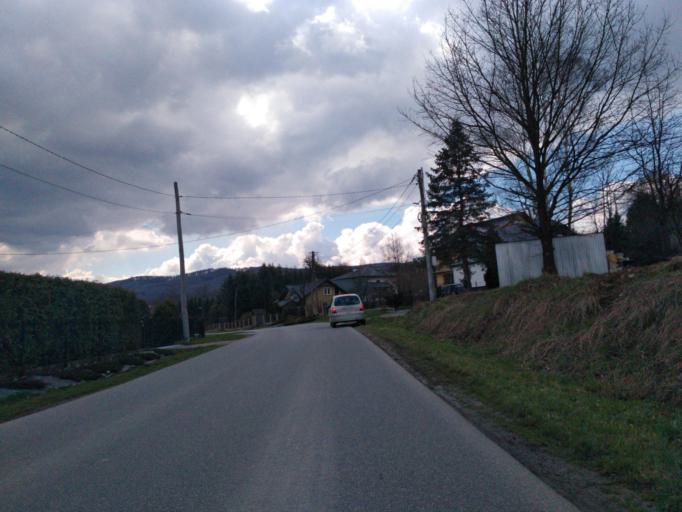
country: PL
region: Subcarpathian Voivodeship
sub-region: Powiat brzozowski
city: Dydnia
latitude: 49.6790
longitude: 22.1842
